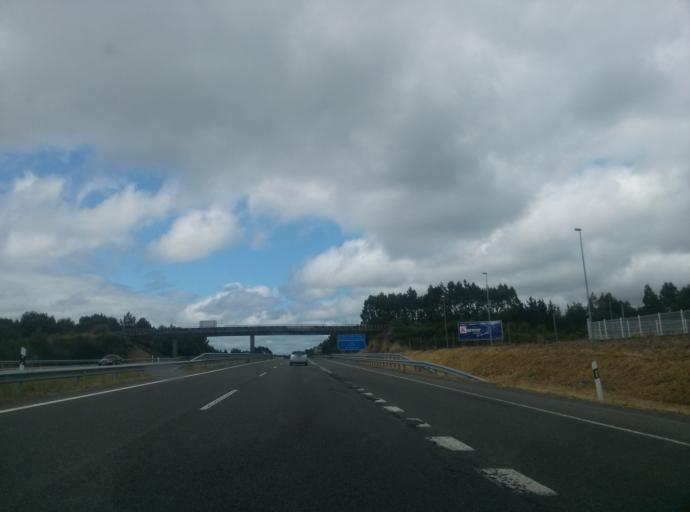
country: ES
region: Galicia
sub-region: Provincia de Lugo
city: Outeiro de Rei
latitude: 43.1092
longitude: -7.6041
